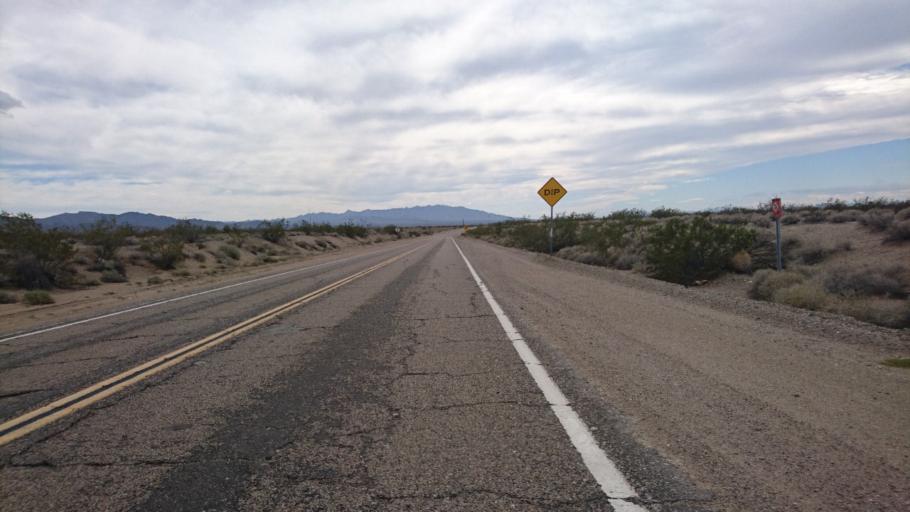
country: US
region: California
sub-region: San Bernardino County
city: Needles
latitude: 34.8087
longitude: -115.1910
